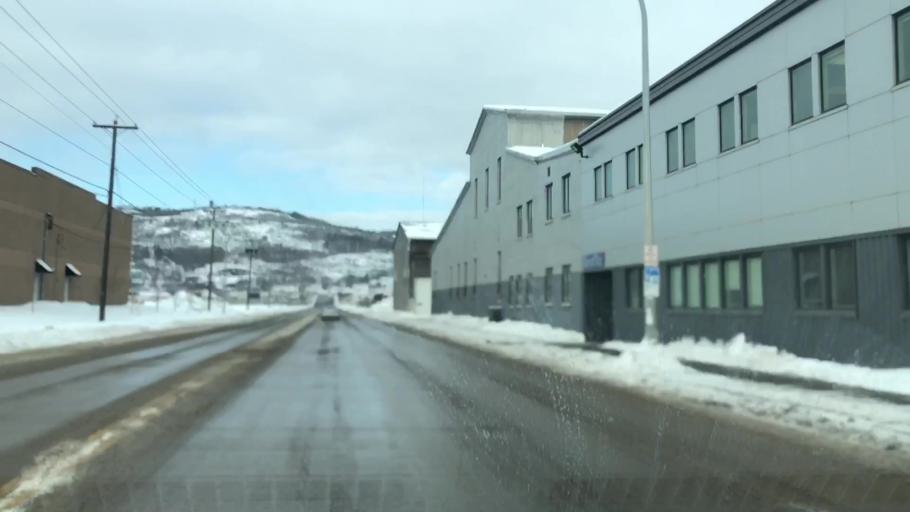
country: US
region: Minnesota
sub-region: Saint Louis County
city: Duluth
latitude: 46.7639
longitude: -92.1124
